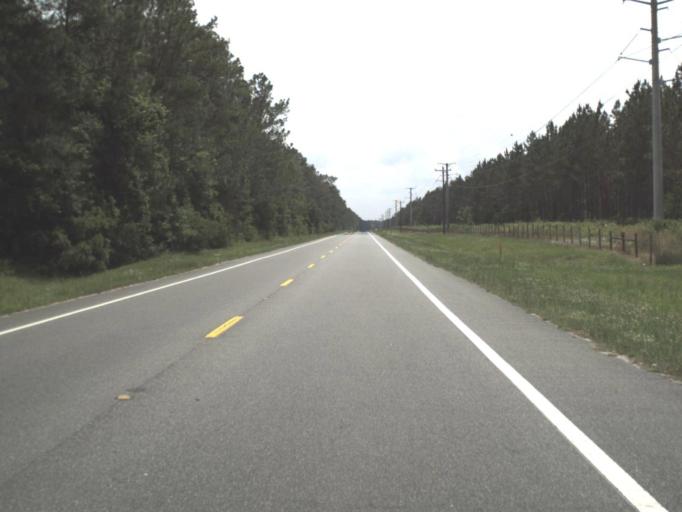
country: US
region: Florida
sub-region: Clay County
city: Asbury Lake
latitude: 29.9319
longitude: -81.8975
